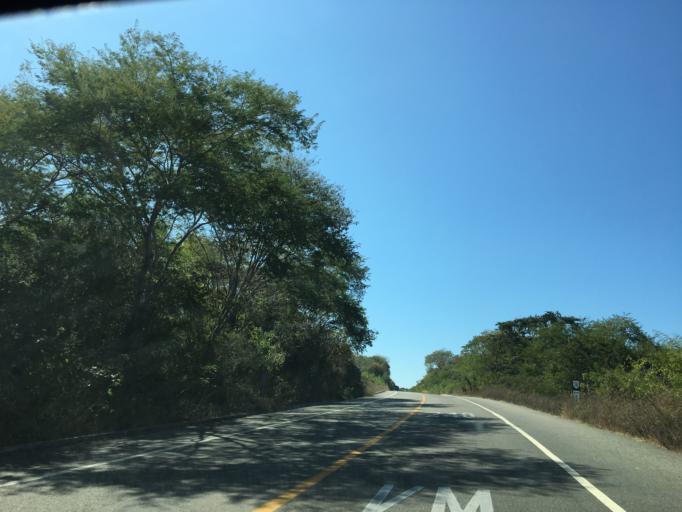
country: MX
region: Oaxaca
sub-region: Santa Maria Huatulco
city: Cuapinolito (Azulillo)
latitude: 15.7740
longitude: -96.2393
